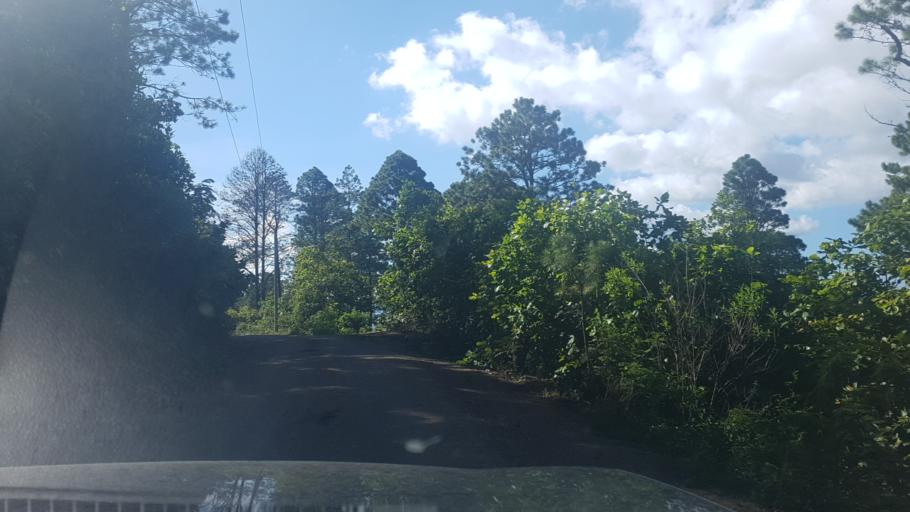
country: NI
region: Nueva Segovia
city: Ocotal
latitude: 13.6435
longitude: -86.6372
